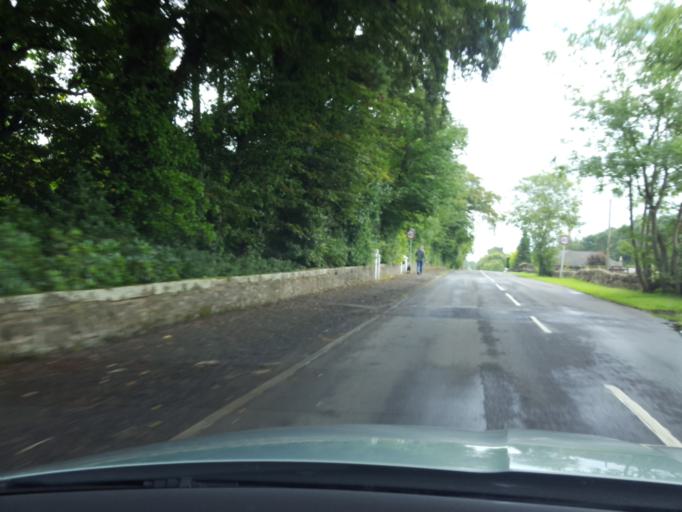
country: GB
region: Scotland
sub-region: Falkirk
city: Polmont
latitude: 55.9614
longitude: -3.6878
